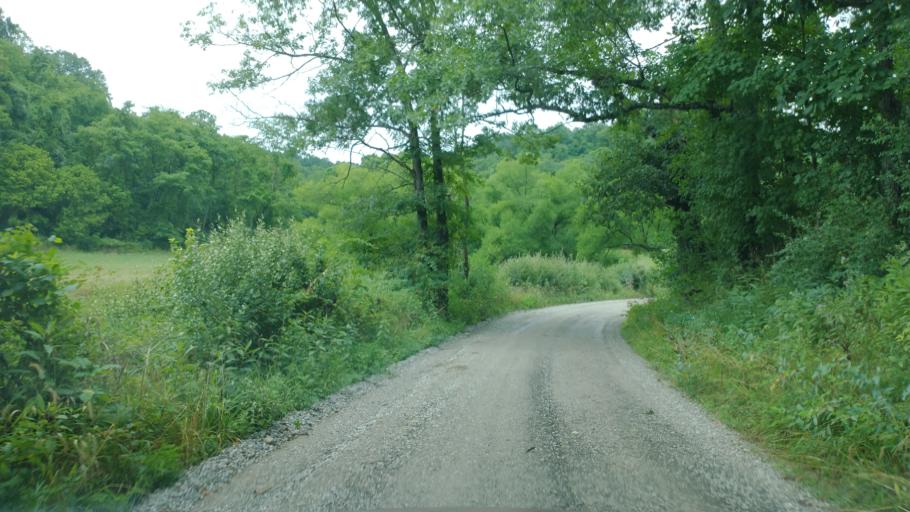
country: US
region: Ohio
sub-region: Meigs County
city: Middleport
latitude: 38.9219
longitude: -82.0507
